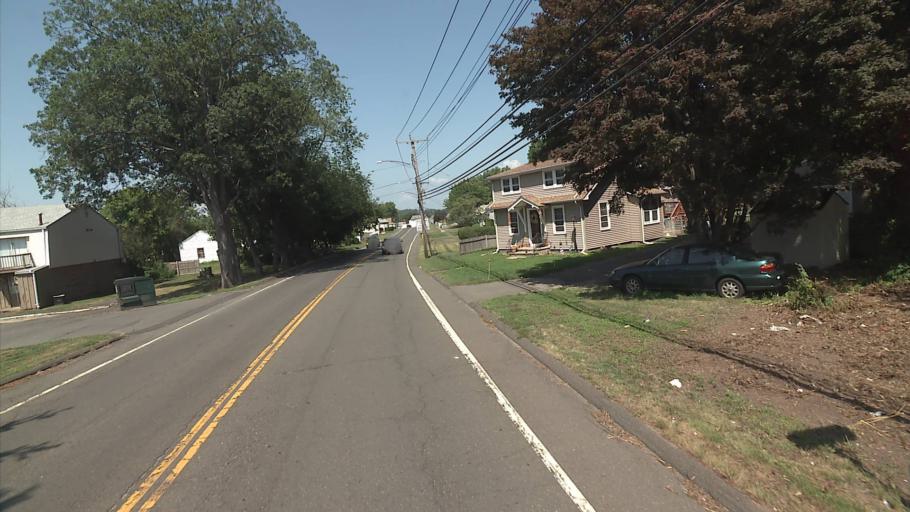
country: US
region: Connecticut
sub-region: New Haven County
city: East Haven
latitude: 41.2623
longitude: -72.8665
